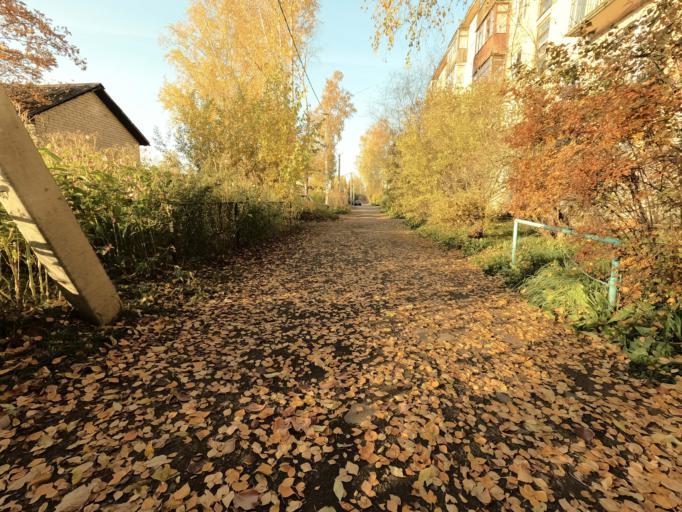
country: RU
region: Leningrad
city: Mga
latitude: 59.7585
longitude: 31.0685
